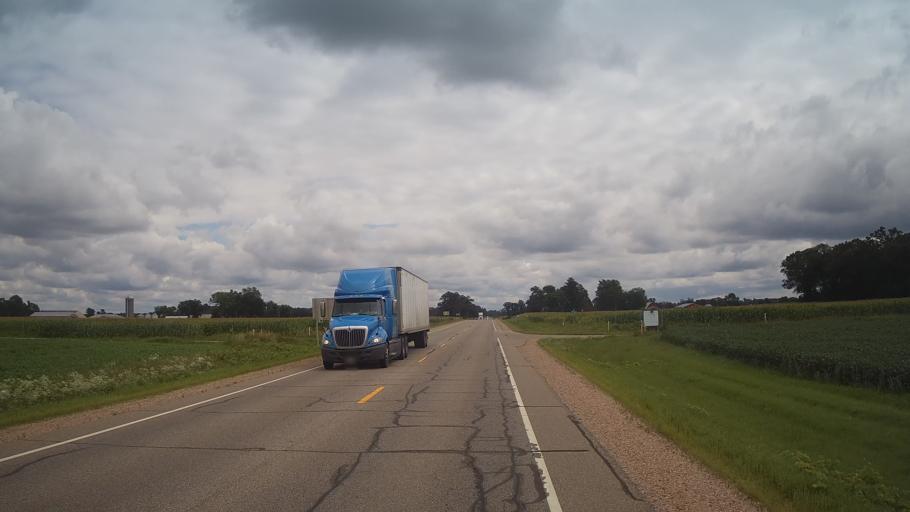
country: US
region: Wisconsin
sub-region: Adams County
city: Friendship
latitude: 44.0393
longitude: -89.9186
